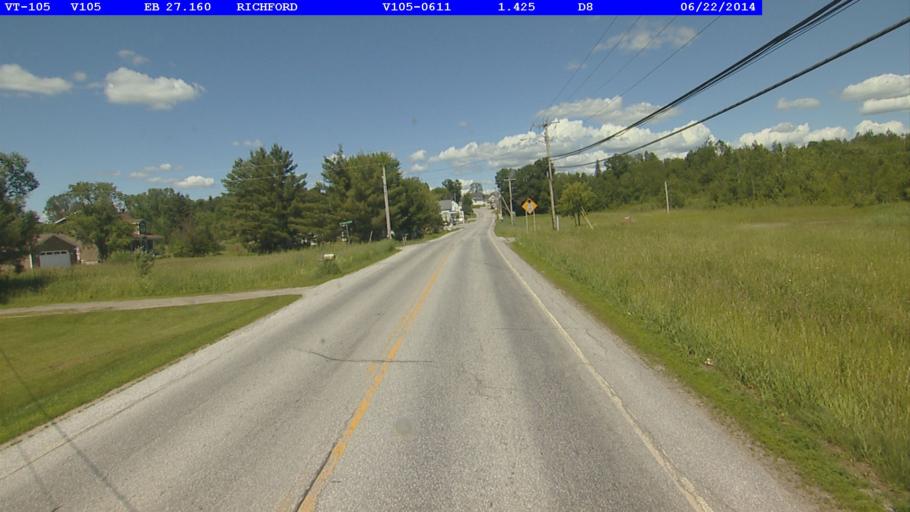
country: US
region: Vermont
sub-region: Franklin County
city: Richford
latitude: 44.9876
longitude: -72.6784
